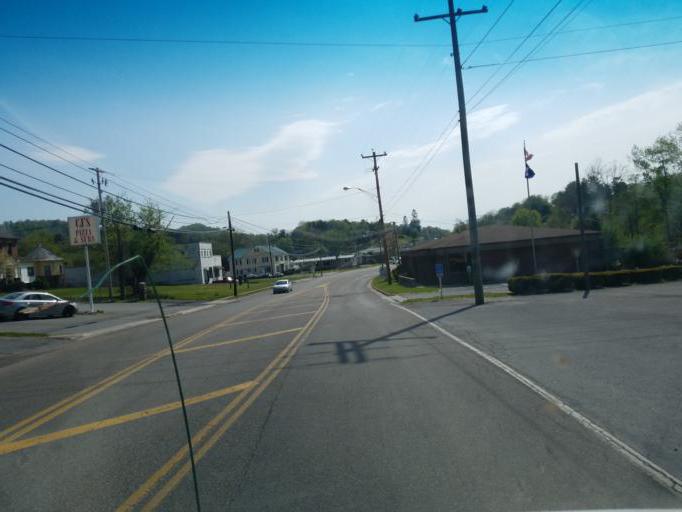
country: US
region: Virginia
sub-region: Smyth County
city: Marion
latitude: 36.8283
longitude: -81.5282
